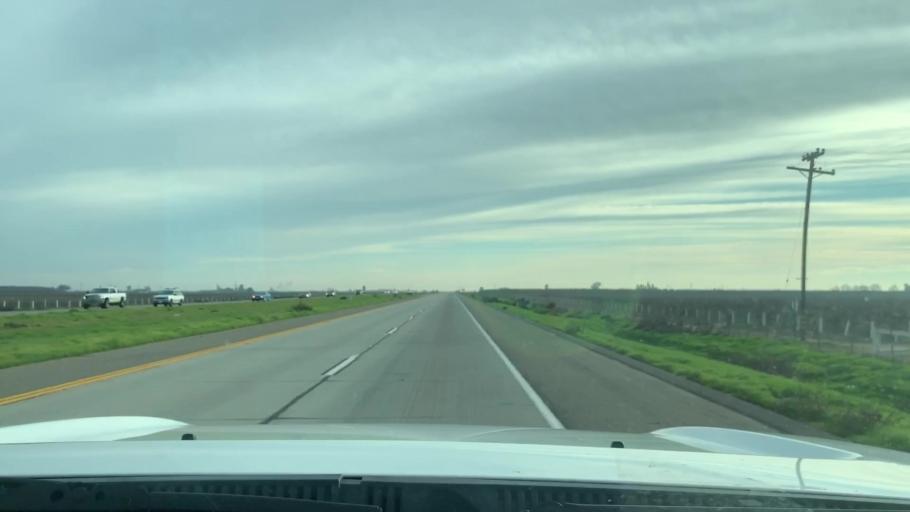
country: US
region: California
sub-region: Fresno County
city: Caruthers
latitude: 36.5837
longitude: -119.7862
